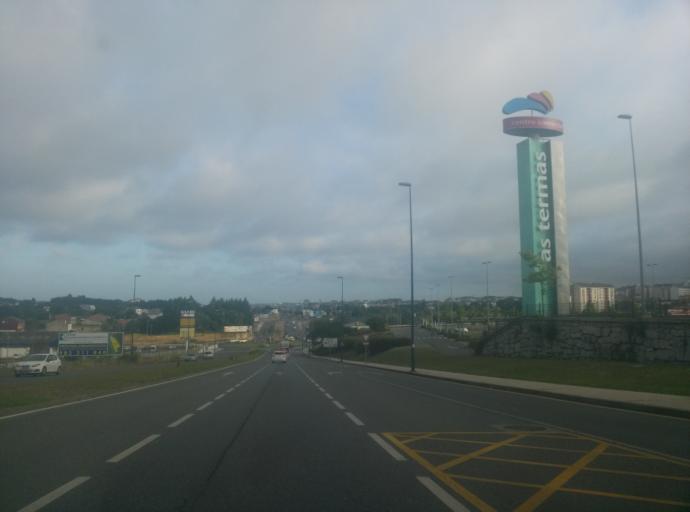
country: ES
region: Galicia
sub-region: Provincia de Lugo
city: Lugo
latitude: 43.0387
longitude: -7.5670
